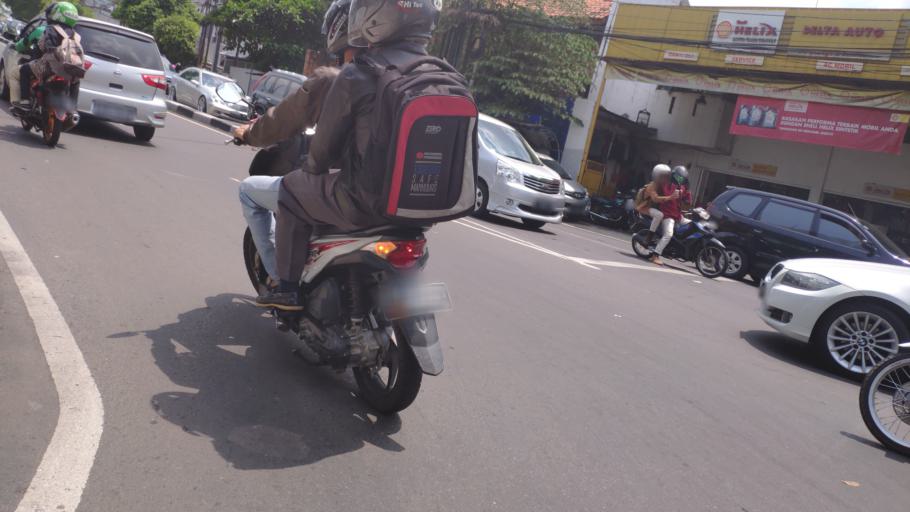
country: ID
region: Jakarta Raya
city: Jakarta
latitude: -6.2758
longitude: 106.8207
